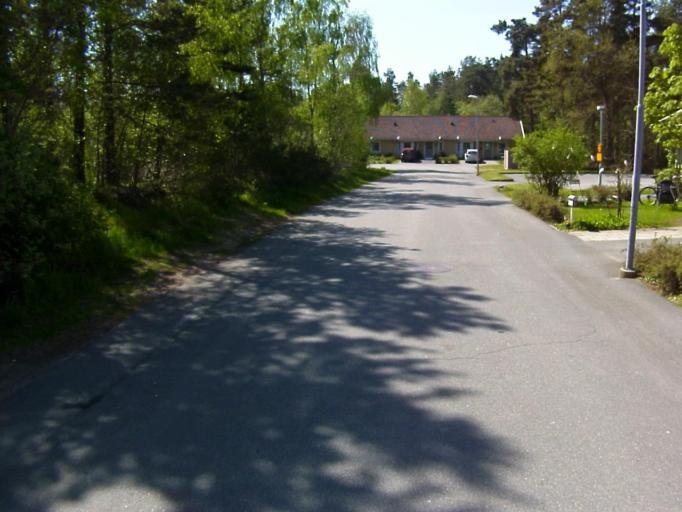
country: SE
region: Skane
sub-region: Kristianstads Kommun
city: Onnestad
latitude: 55.9429
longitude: 13.9764
